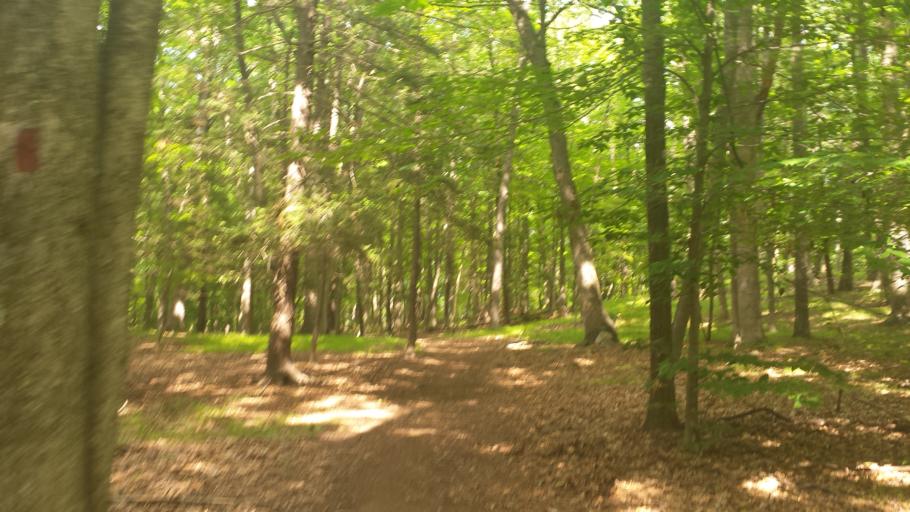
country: US
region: New York
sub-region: Westchester County
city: Yorktown Heights
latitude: 41.2234
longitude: -73.7812
